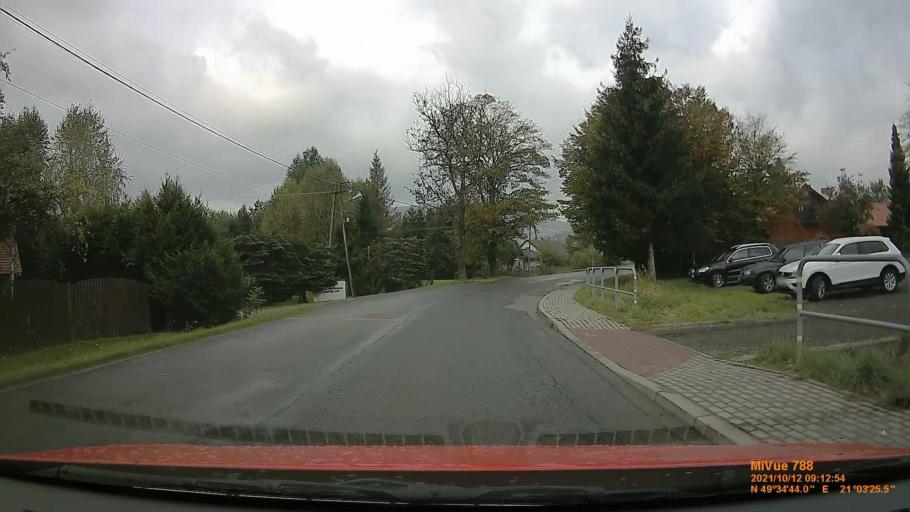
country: PL
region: Lesser Poland Voivodeship
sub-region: Powiat gorlicki
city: Ropa
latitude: 49.5789
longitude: 21.0569
